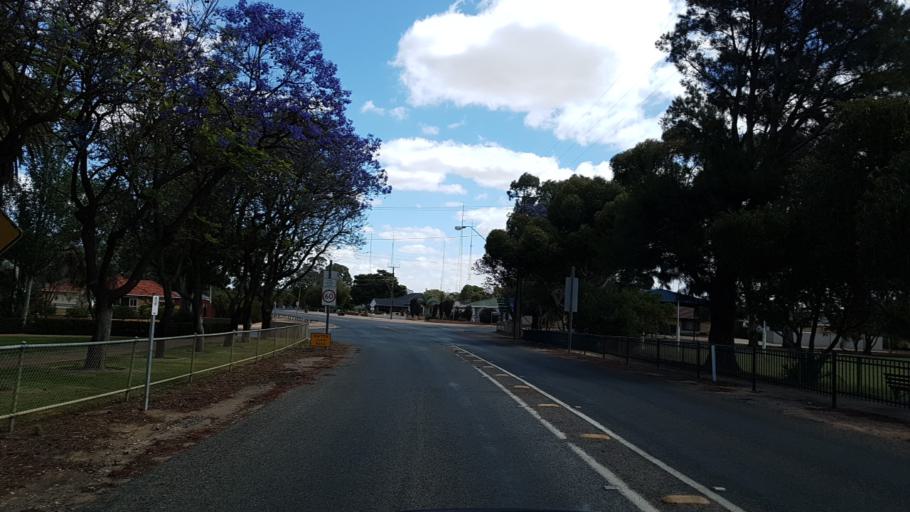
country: AU
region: South Australia
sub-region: Loxton Waikerie
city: Waikerie
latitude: -34.1821
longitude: 139.9819
